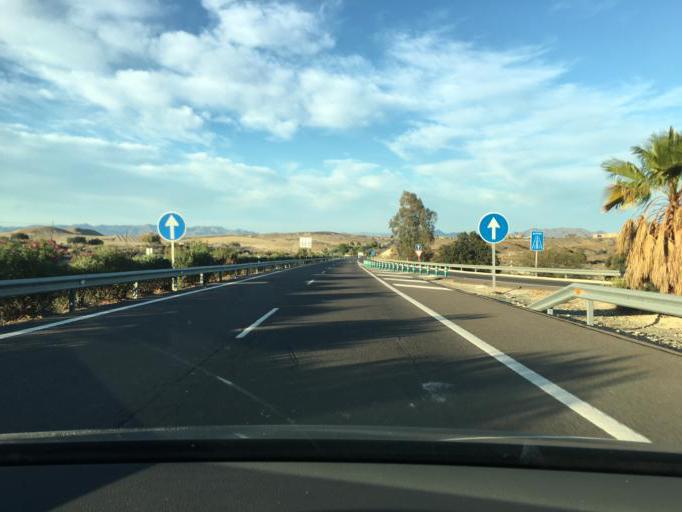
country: ES
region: Andalusia
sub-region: Provincia de Almeria
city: Turre
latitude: 37.1931
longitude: -1.9152
